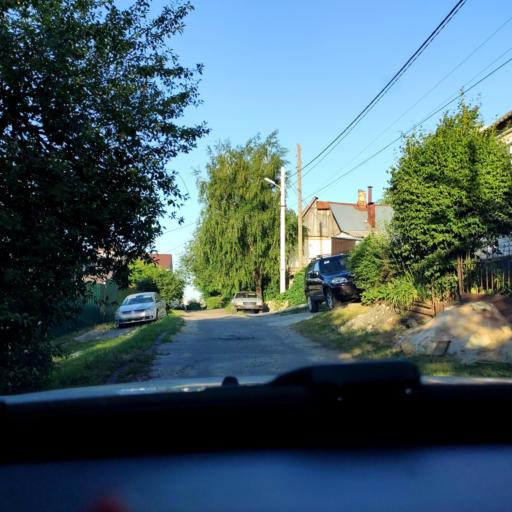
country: RU
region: Voronezj
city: Voronezh
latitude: 51.6379
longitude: 39.1965
